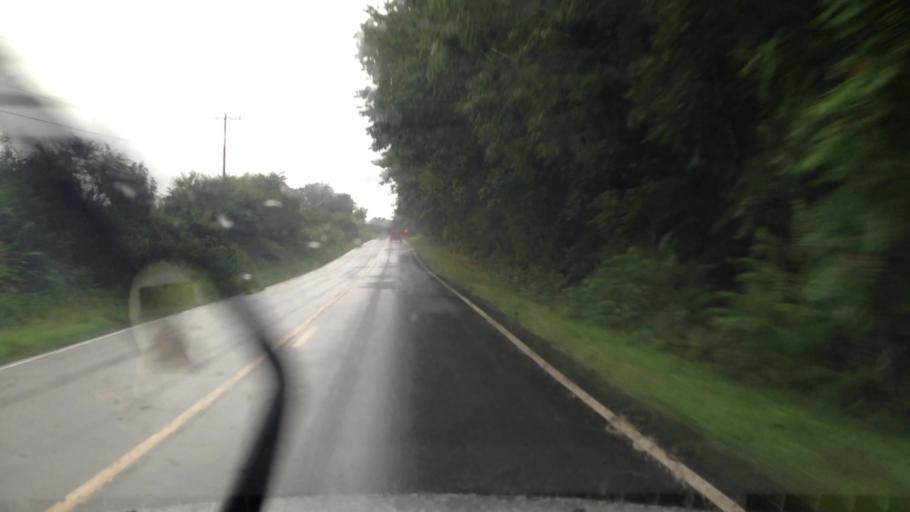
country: US
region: North Carolina
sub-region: Rockingham County
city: Reidsville
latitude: 36.2854
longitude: -79.7363
